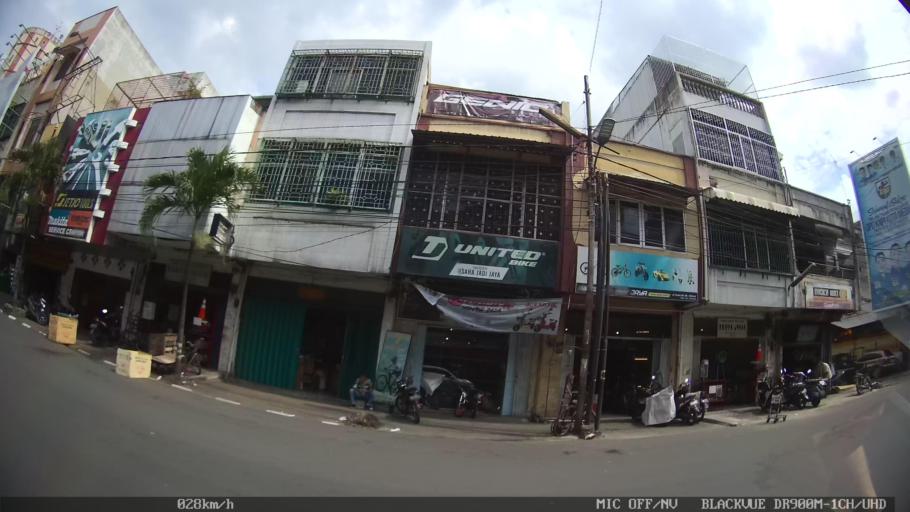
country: ID
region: North Sumatra
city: Medan
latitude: 3.5822
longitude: 98.6842
